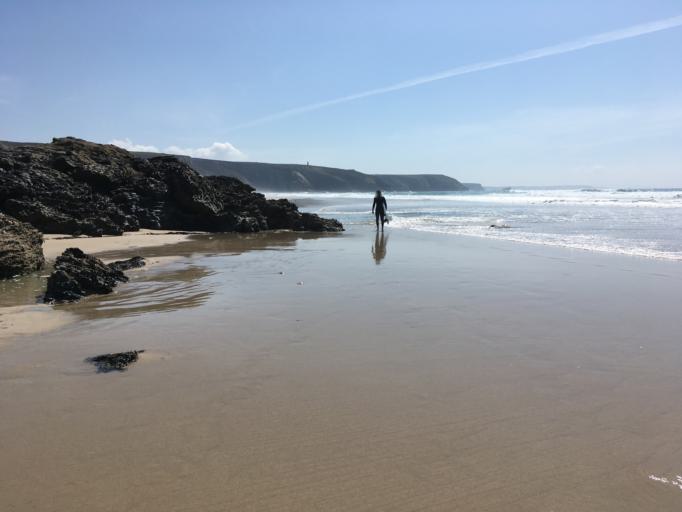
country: GB
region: England
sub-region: Cornwall
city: Saint Agnes
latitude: 50.2935
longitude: -5.2424
